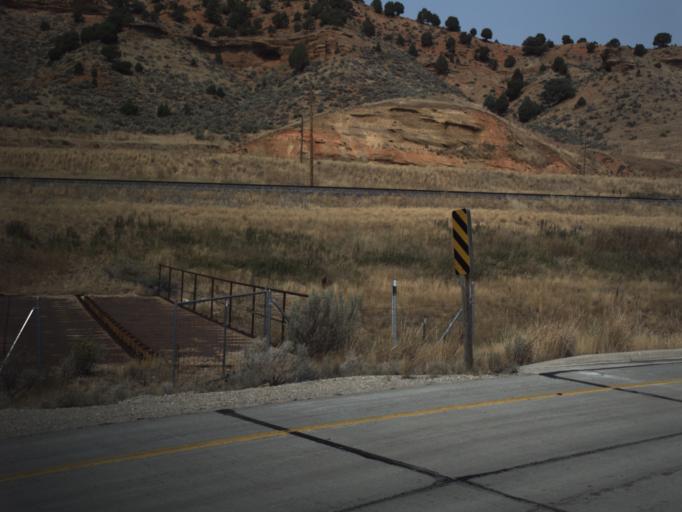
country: US
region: Utah
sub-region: Summit County
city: Coalville
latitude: 41.0808
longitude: -111.2475
